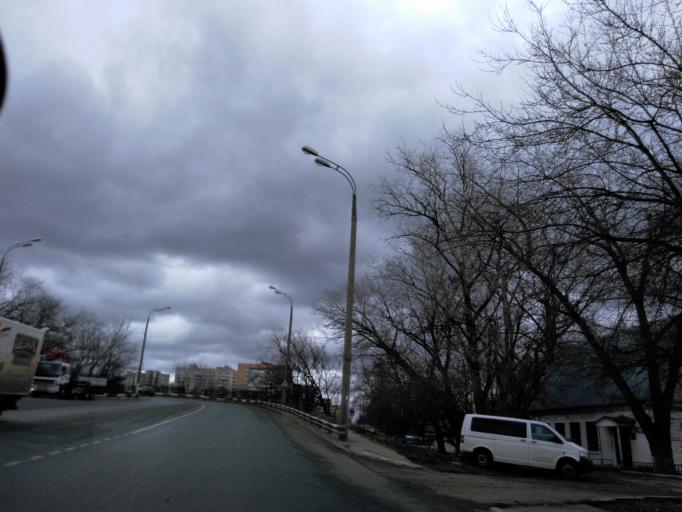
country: RU
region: Moskovskaya
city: Koptevo
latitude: 55.8414
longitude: 37.5194
